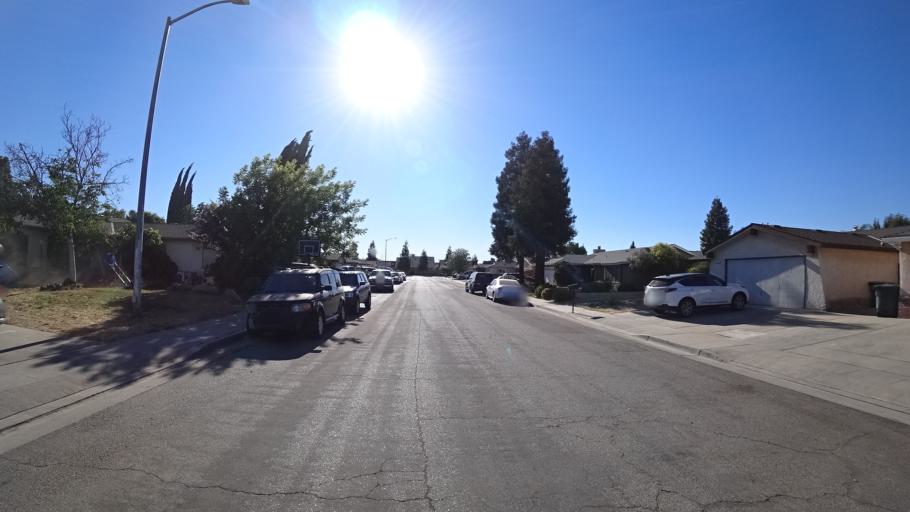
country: US
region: California
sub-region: Fresno County
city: West Park
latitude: 36.7817
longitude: -119.8683
